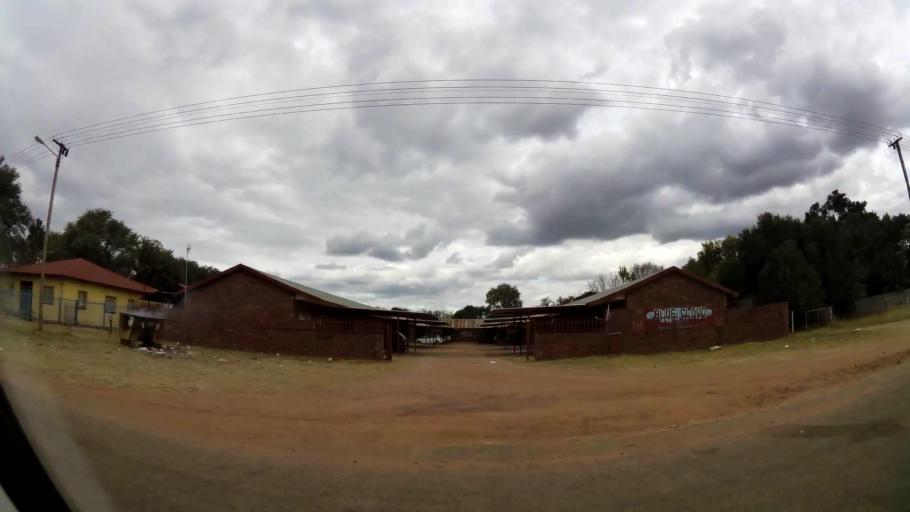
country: ZA
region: Limpopo
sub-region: Waterberg District Municipality
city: Modimolle
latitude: -24.7061
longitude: 28.4147
